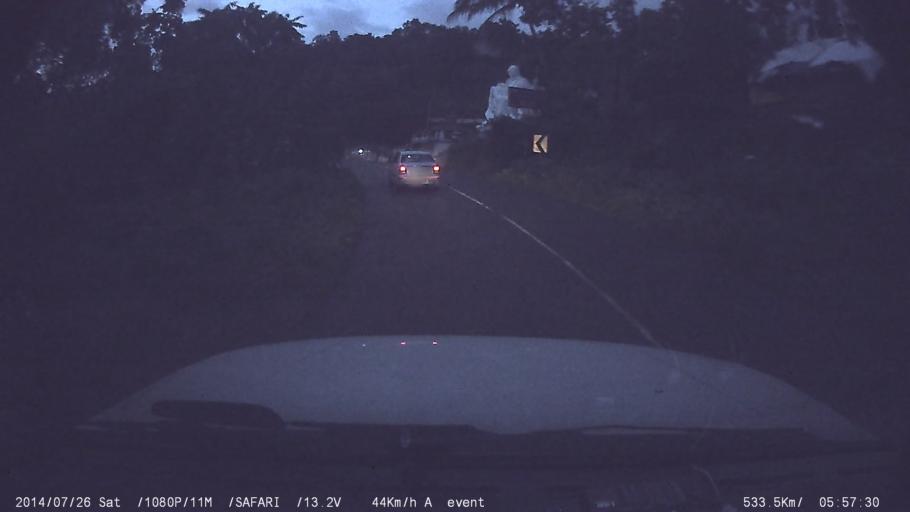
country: IN
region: Kerala
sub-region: Ernakulam
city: Muvattupuzha
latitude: 9.9298
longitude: 76.5770
